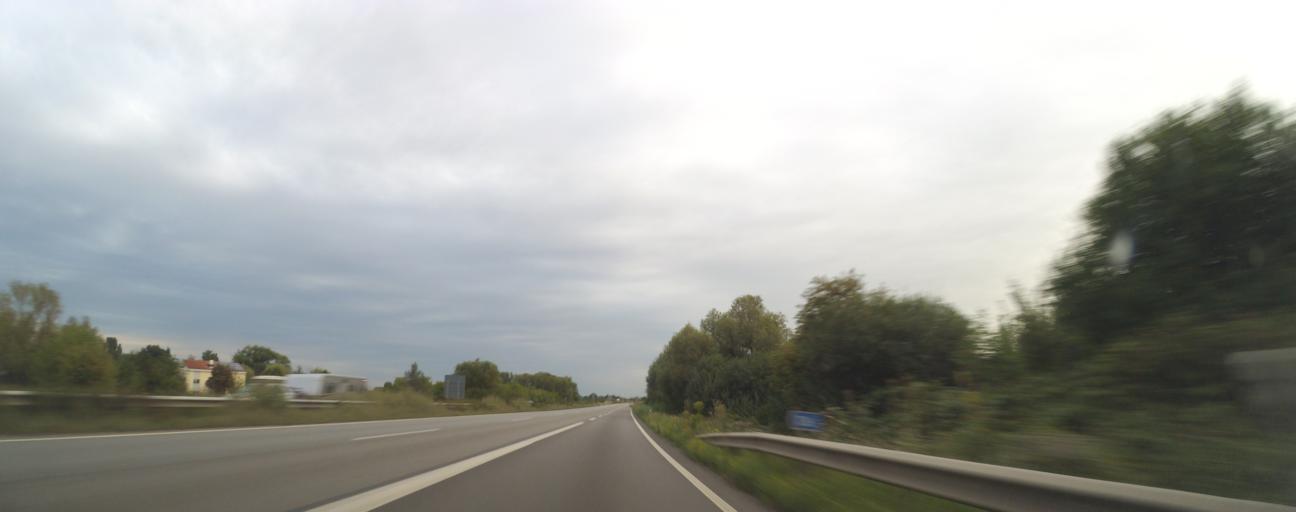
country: DE
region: Rheinland-Pfalz
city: Kirrweiler
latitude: 49.2849
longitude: 8.1529
